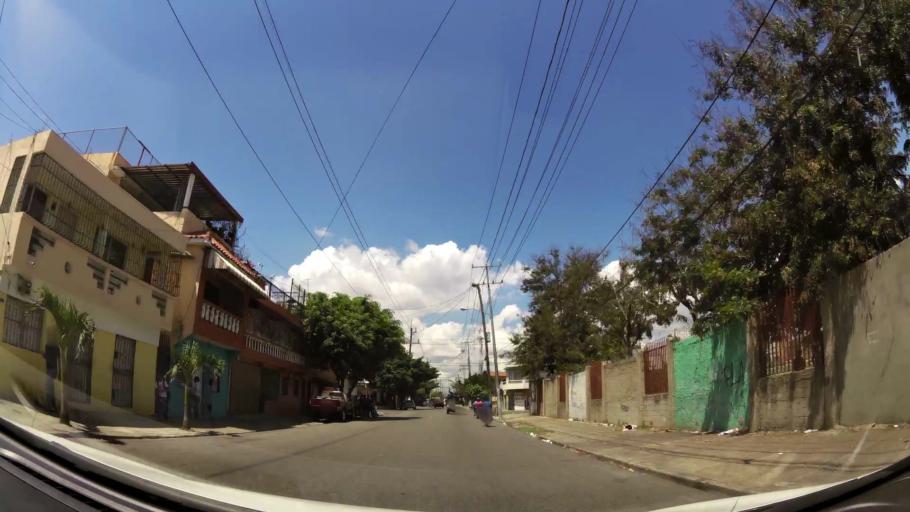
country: DO
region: Nacional
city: San Carlos
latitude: 18.4913
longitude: -69.8911
